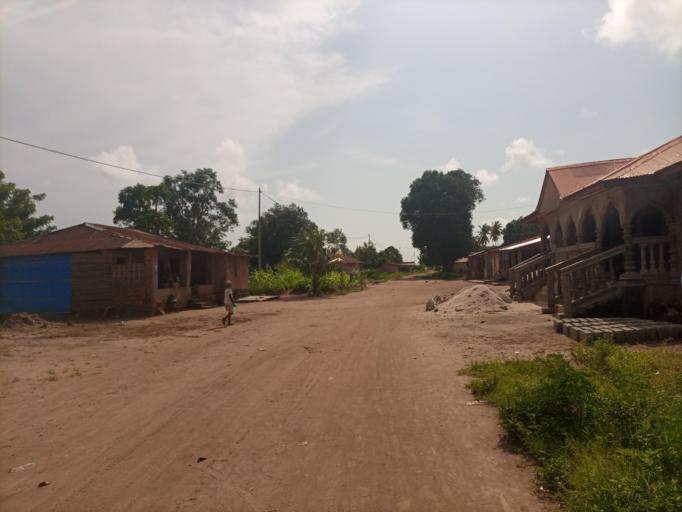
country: SL
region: Northern Province
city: Masoyila
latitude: 8.6105
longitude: -13.1730
